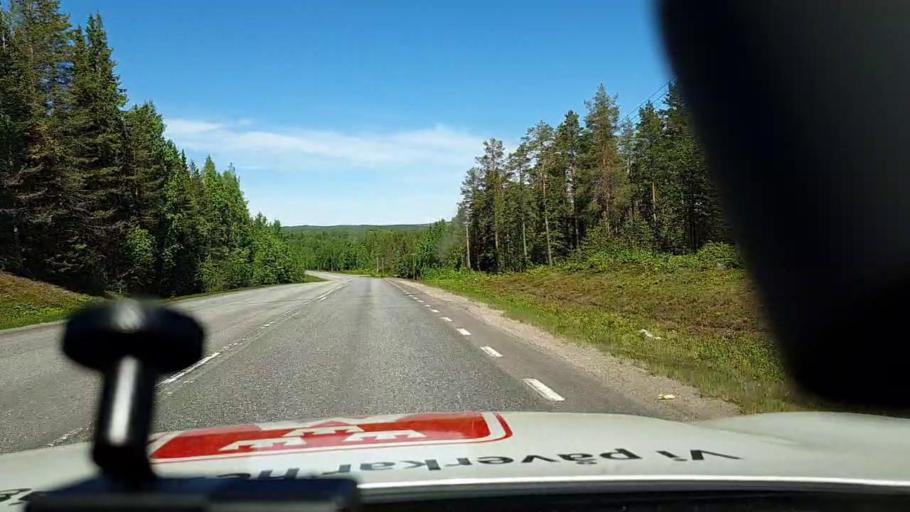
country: SE
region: Norrbotten
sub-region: Kalix Kommun
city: Toere
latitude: 66.1004
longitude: 22.7122
